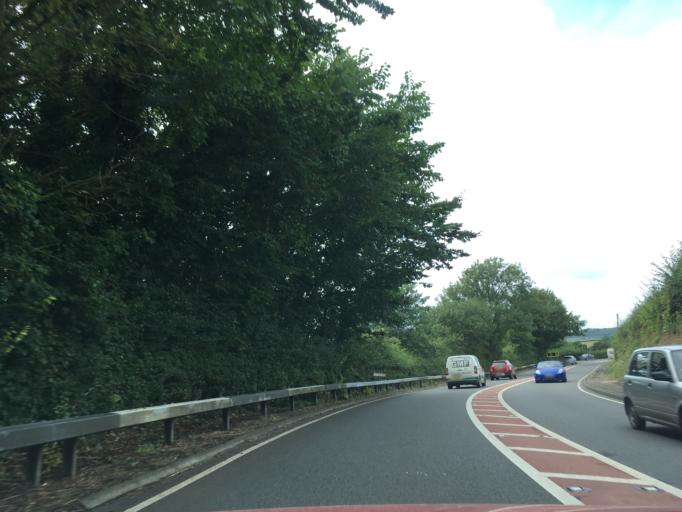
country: GB
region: Wales
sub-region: Carmarthenshire
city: Llanddarog
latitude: 51.8693
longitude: -4.1296
